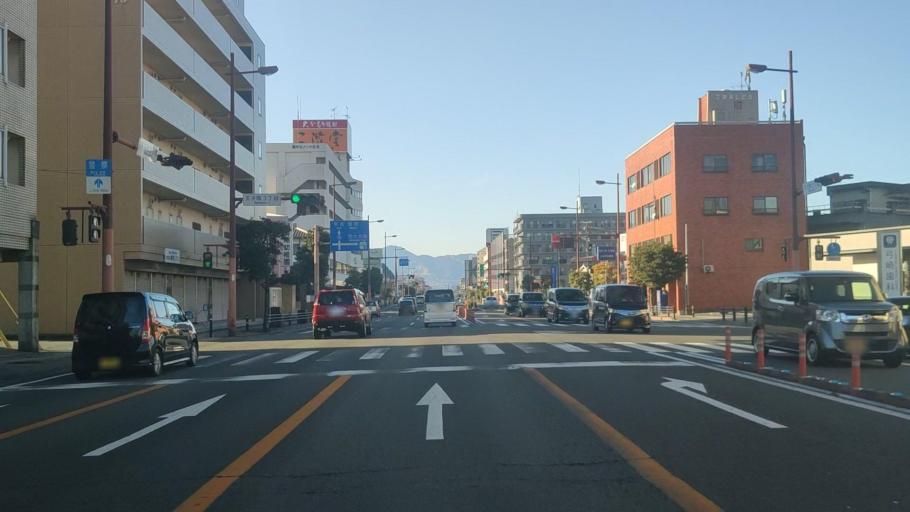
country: JP
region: Oita
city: Oita
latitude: 33.2428
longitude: 131.5899
